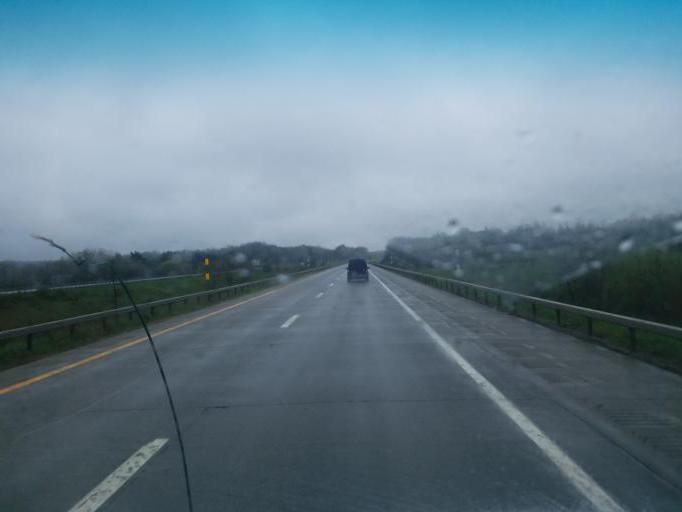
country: US
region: New York
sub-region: Chautauqua County
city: Mayville
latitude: 42.1547
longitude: -79.4974
